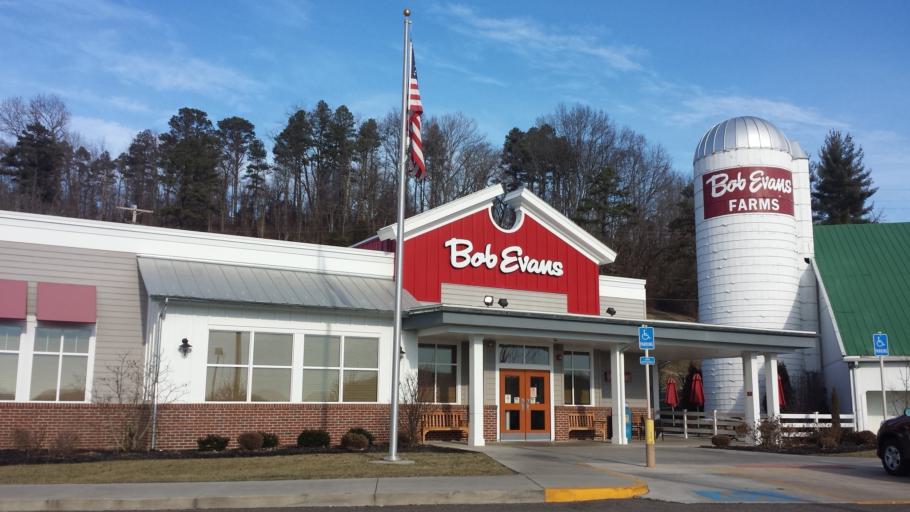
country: US
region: Ohio
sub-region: Gallia County
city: Gallipolis
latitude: 38.8823
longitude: -82.3682
